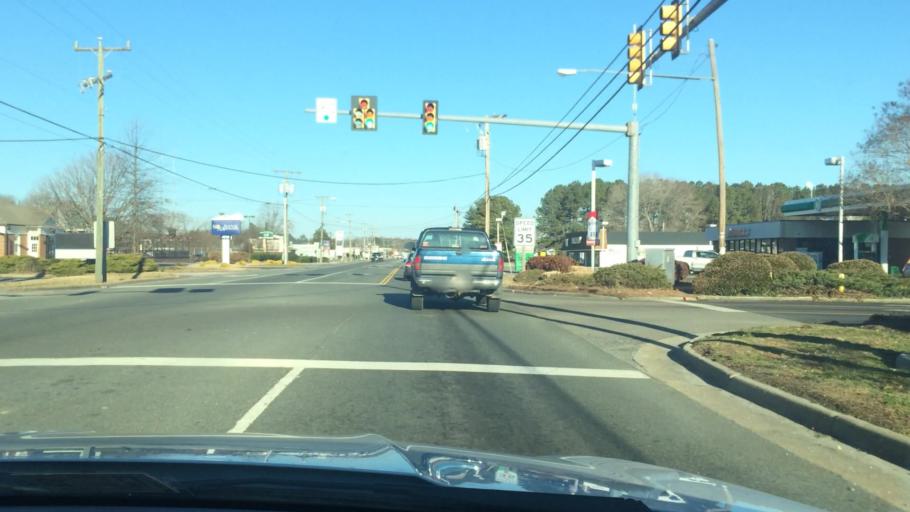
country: US
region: Virginia
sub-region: Lancaster County
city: Kilmarnock
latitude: 37.7198
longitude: -76.3845
